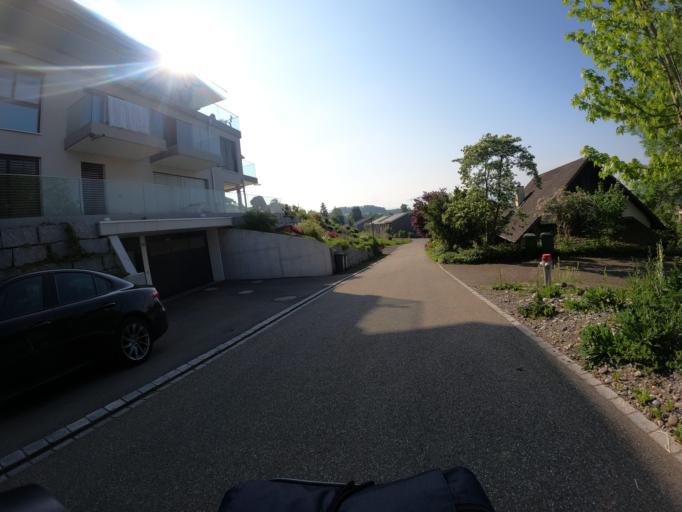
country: CH
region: Zurich
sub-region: Bezirk Affoltern
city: Mettmenstetten
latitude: 47.2500
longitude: 8.4639
